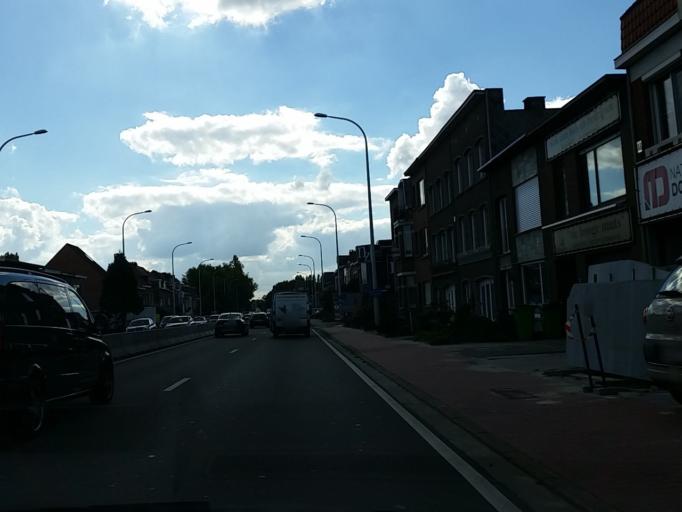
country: BE
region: Flanders
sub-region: Provincie Antwerpen
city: Wijnegem
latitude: 51.2209
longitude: 4.4978
